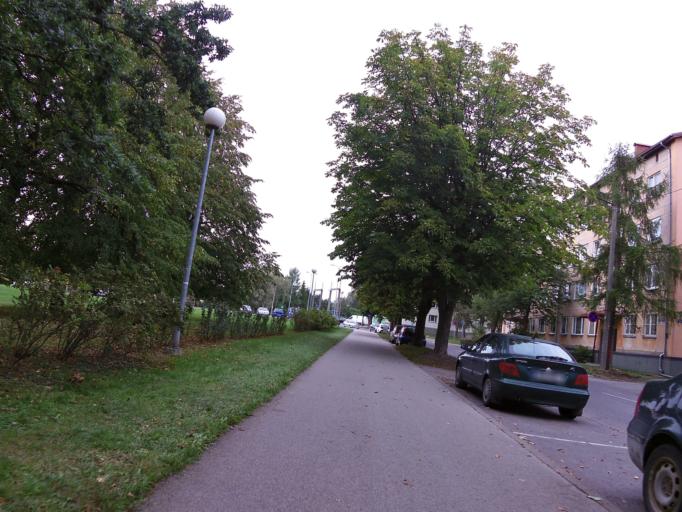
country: EE
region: Harju
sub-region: Tallinna linn
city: Tallinn
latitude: 59.4496
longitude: 24.6855
